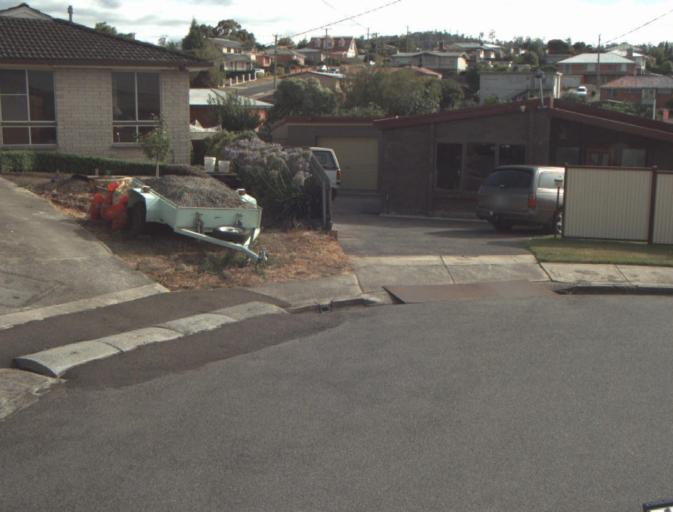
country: AU
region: Tasmania
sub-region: Launceston
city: Invermay
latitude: -41.3929
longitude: 147.1324
